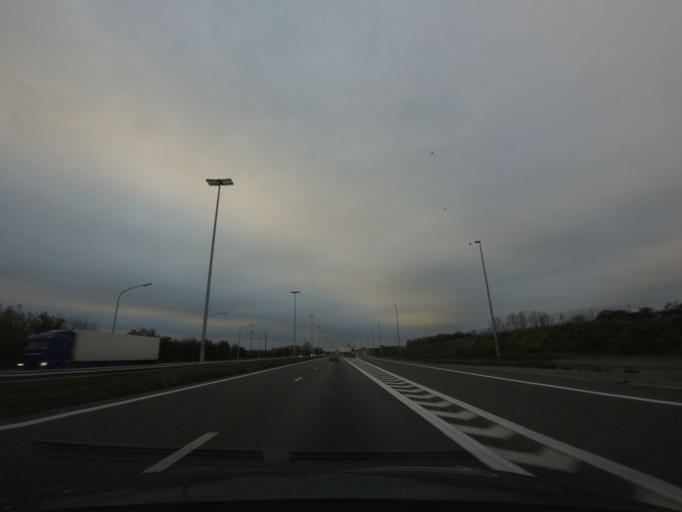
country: BE
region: Flanders
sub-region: Provincie Antwerpen
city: Hoogstraten
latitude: 51.4261
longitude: 4.7087
